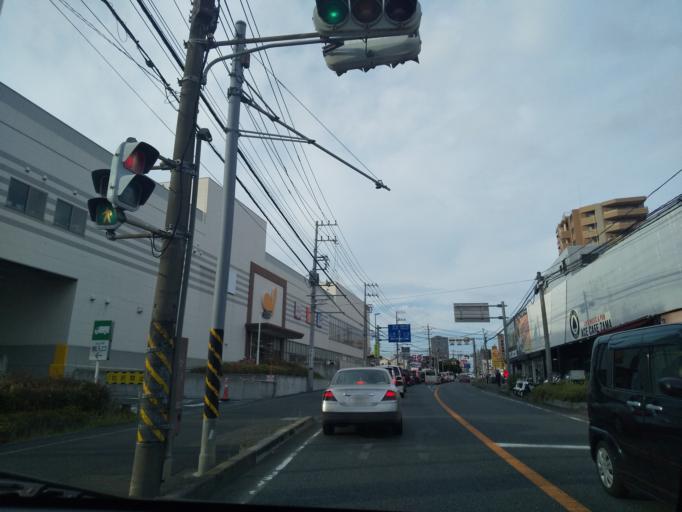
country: JP
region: Kanagawa
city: Zama
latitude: 35.5074
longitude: 139.4136
